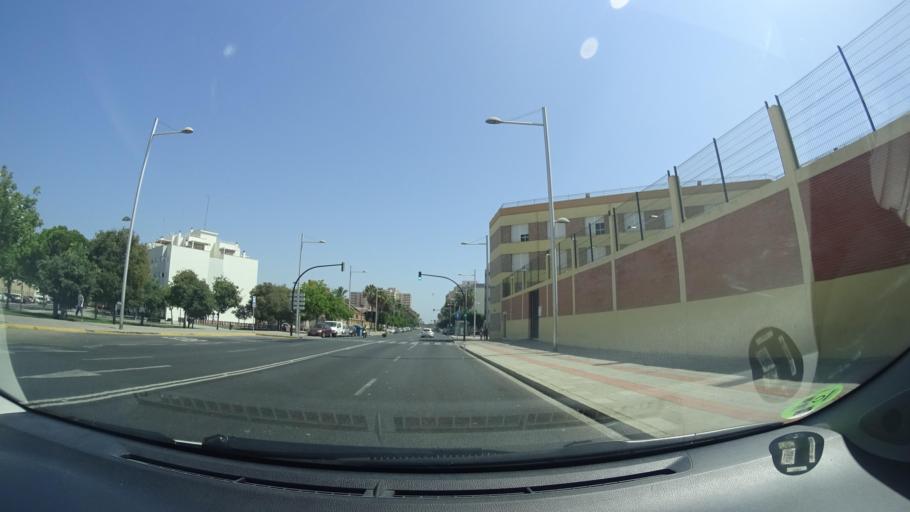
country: ES
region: Andalusia
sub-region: Provincia de Cadiz
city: Cadiz
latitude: 36.5087
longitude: -6.2748
